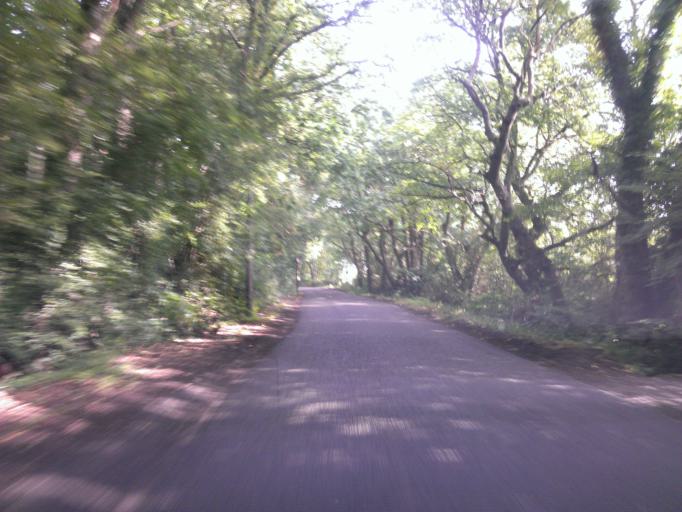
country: GB
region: England
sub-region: Essex
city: Saint Osyth
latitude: 51.8338
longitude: 1.1034
